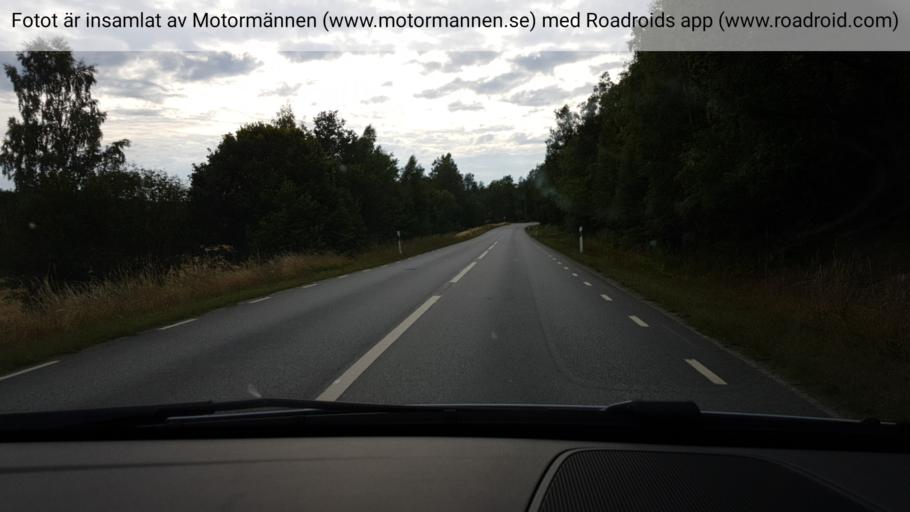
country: SE
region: Stockholm
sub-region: Norrtalje Kommun
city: Skanninge
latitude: 59.8939
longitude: 18.4642
